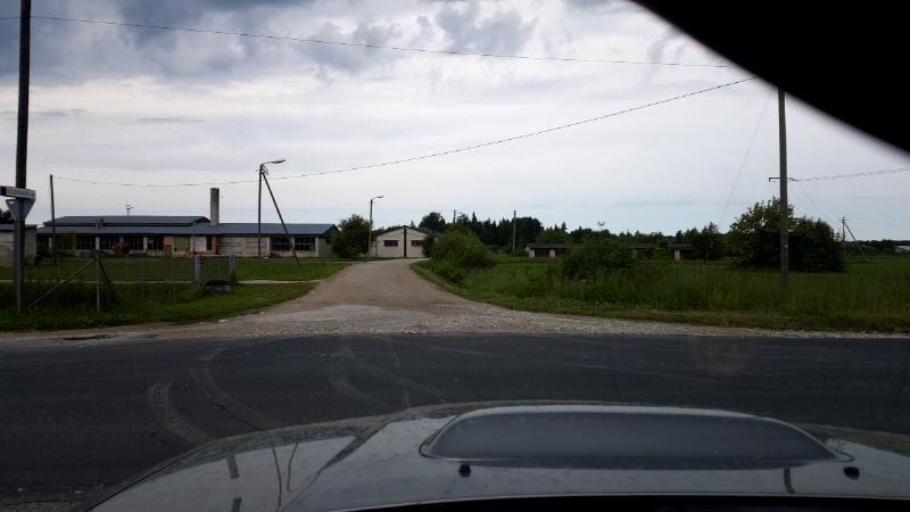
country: EE
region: Paernumaa
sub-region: Tootsi vald
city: Tootsi
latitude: 58.5288
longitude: 24.7042
